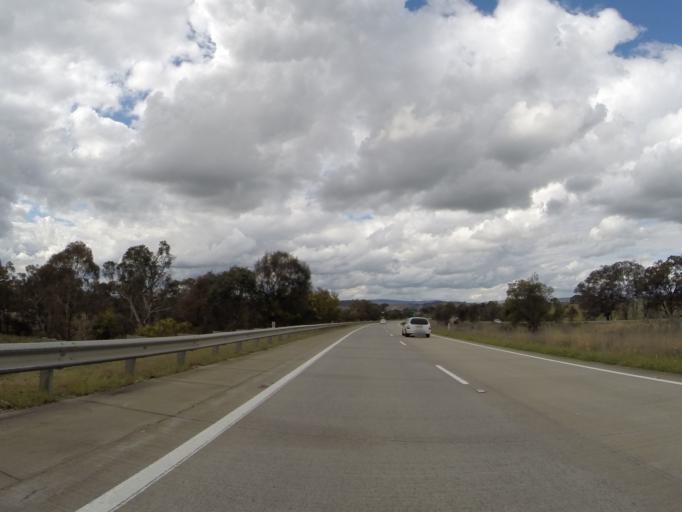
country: AU
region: New South Wales
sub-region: Yass Valley
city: Gundaroo
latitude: -34.7870
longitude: 149.2399
